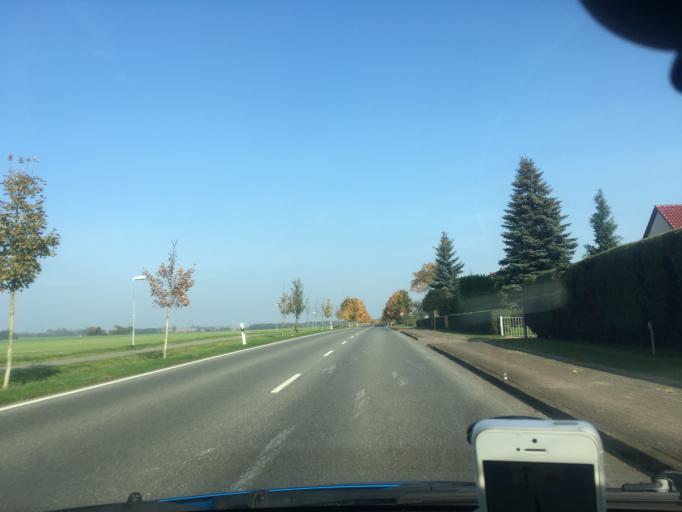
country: DE
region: Mecklenburg-Vorpommern
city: Stralendorf
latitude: 53.5331
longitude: 11.3029
